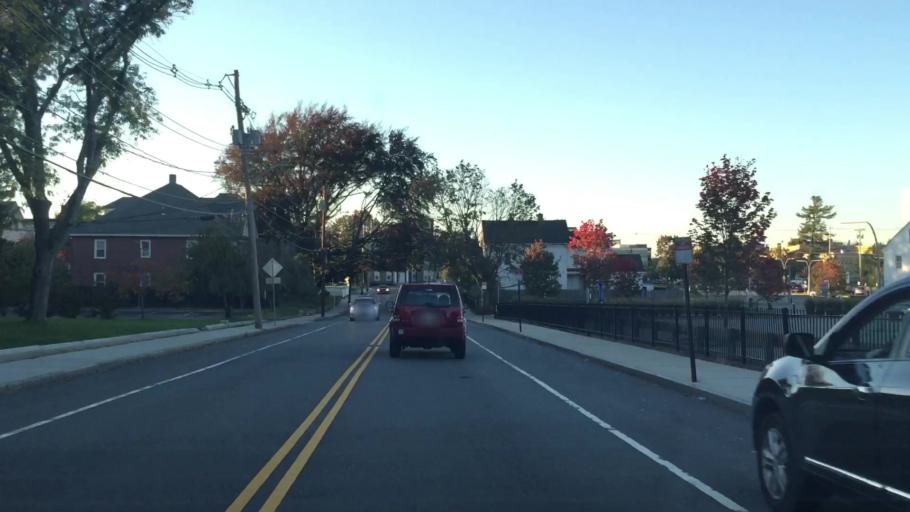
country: US
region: Massachusetts
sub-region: Middlesex County
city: Lowell
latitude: 42.6483
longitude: -71.3243
